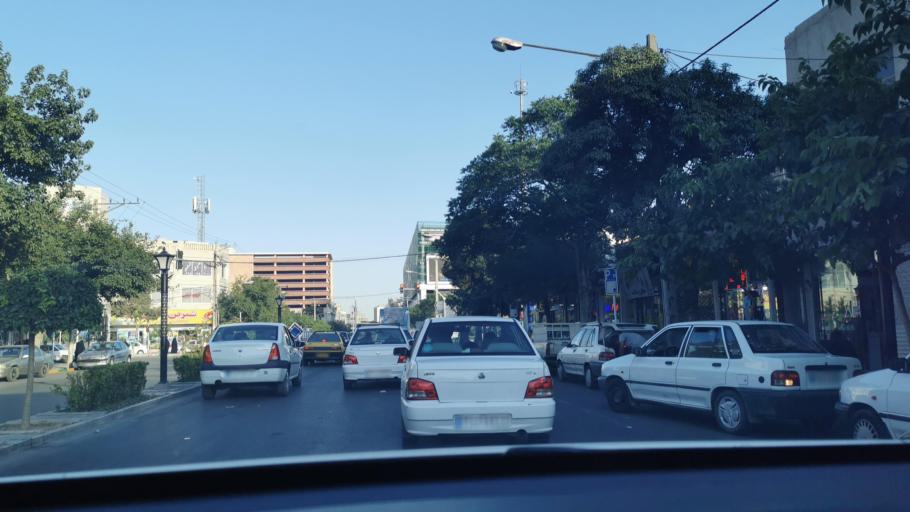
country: IR
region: Razavi Khorasan
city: Mashhad
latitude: 36.2939
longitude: 59.6454
